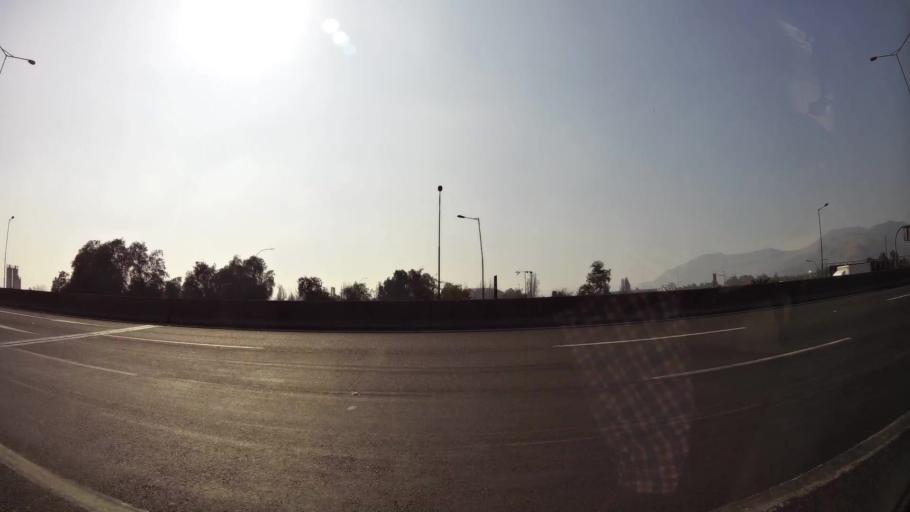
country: CL
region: Santiago Metropolitan
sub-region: Provincia de Santiago
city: Lo Prado
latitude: -33.3666
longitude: -70.7008
